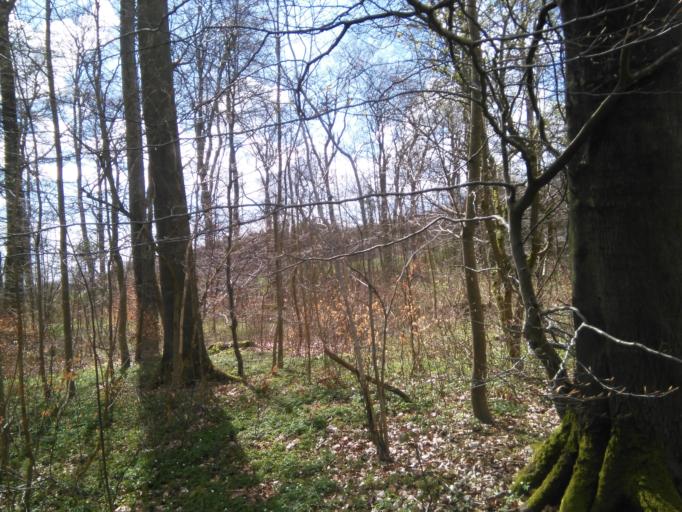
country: DK
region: Central Jutland
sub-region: Arhus Kommune
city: Trige
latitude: 56.2365
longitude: 10.1786
